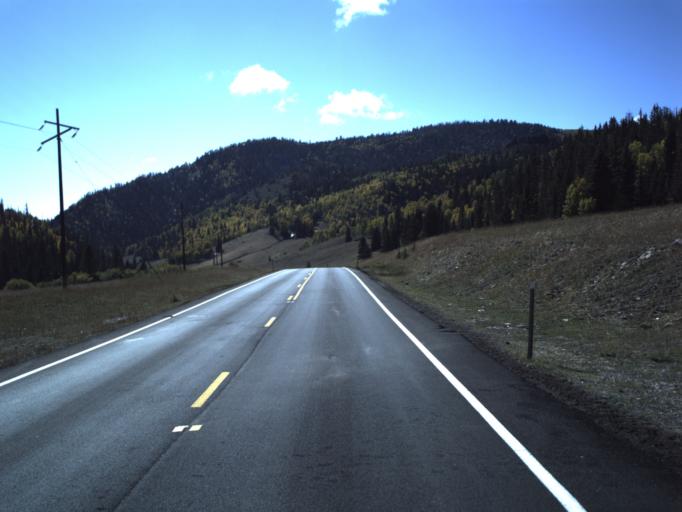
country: US
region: Utah
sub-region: Beaver County
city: Beaver
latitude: 38.3010
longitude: -112.4319
